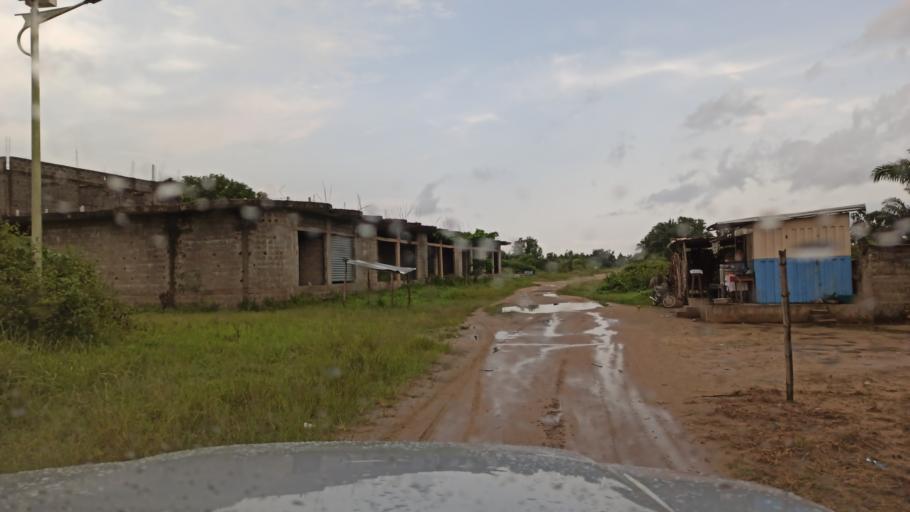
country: BJ
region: Queme
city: Porto-Novo
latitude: 6.4510
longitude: 2.6643
